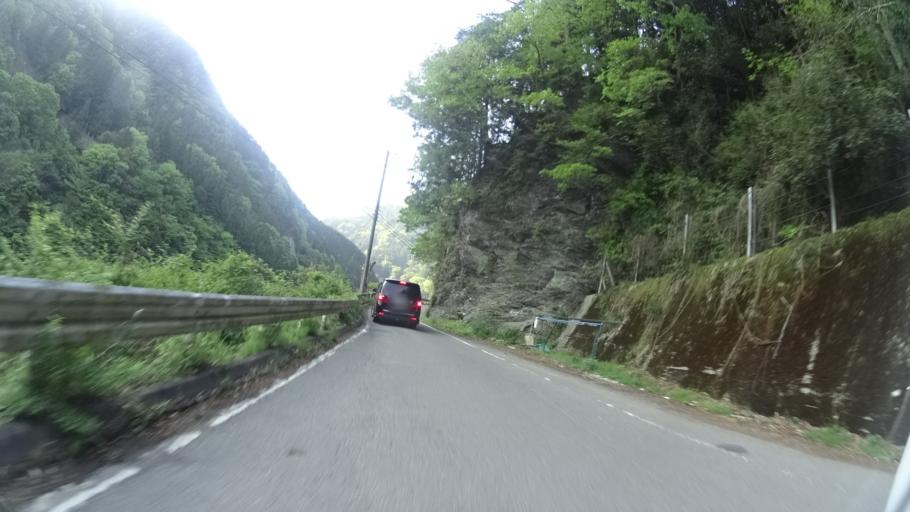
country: JP
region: Tokushima
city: Ikedacho
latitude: 33.8733
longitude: 133.8699
